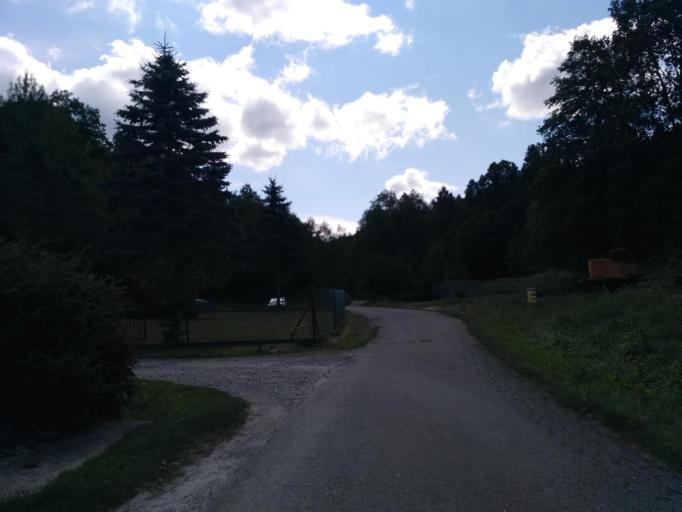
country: PL
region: Subcarpathian Voivodeship
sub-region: Powiat strzyzowski
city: Polomia
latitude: 49.9150
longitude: 21.8839
